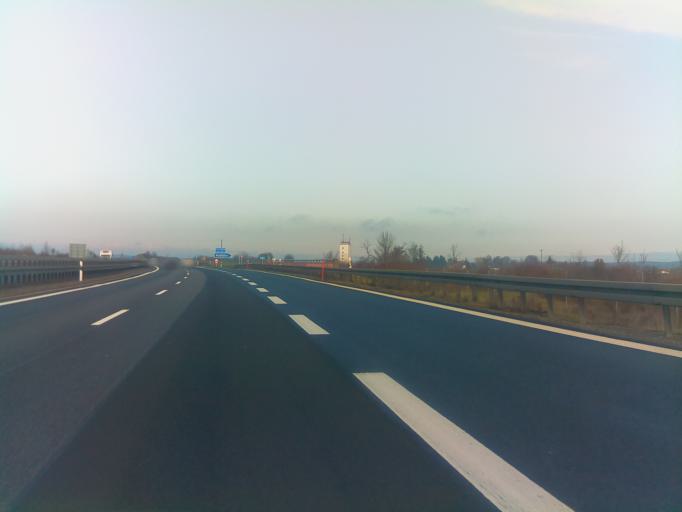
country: DE
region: Bavaria
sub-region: Regierungsbezirk Unterfranken
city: Euerbach
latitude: 50.0588
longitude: 10.1508
